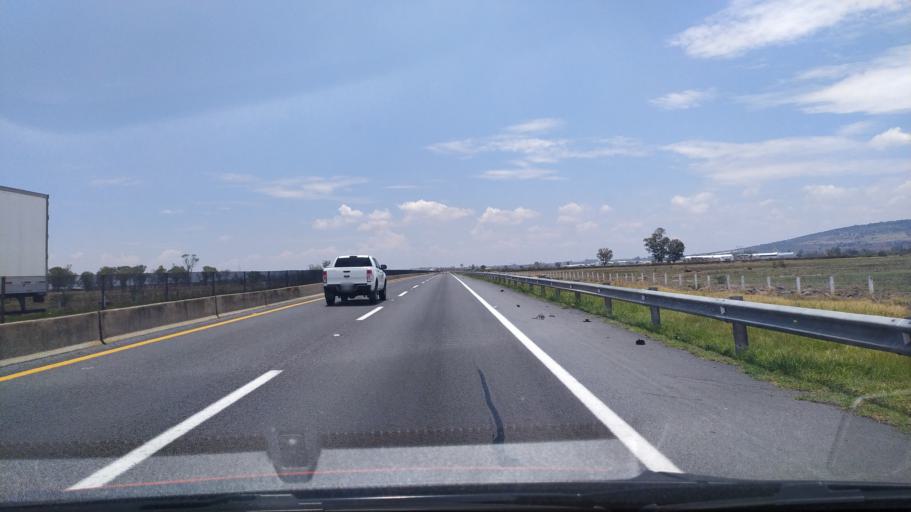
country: MX
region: Jalisco
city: Tepatitlan de Morelos
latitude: 20.9061
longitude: -102.6880
